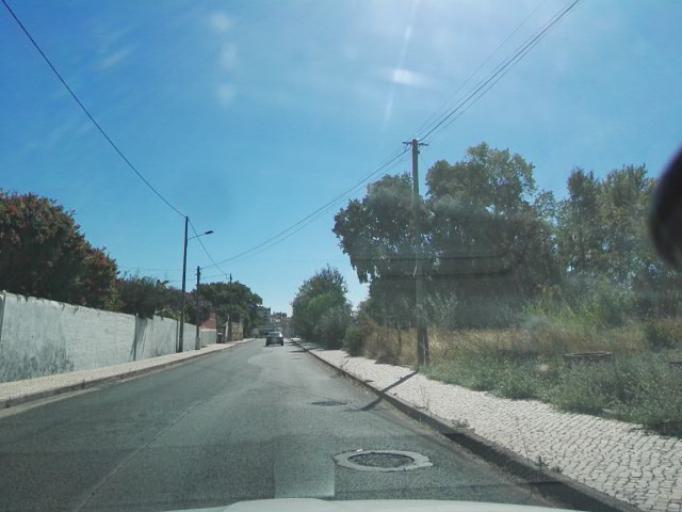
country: PT
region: Lisbon
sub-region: Vila Franca de Xira
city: Alhandra
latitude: 38.9307
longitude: -9.0156
